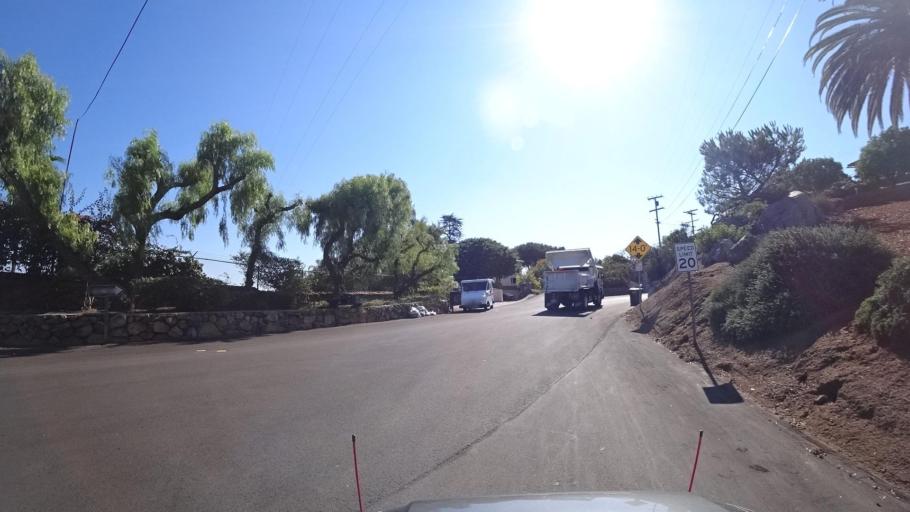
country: US
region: California
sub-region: San Diego County
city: Casa de Oro-Mount Helix
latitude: 32.7691
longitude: -116.9819
